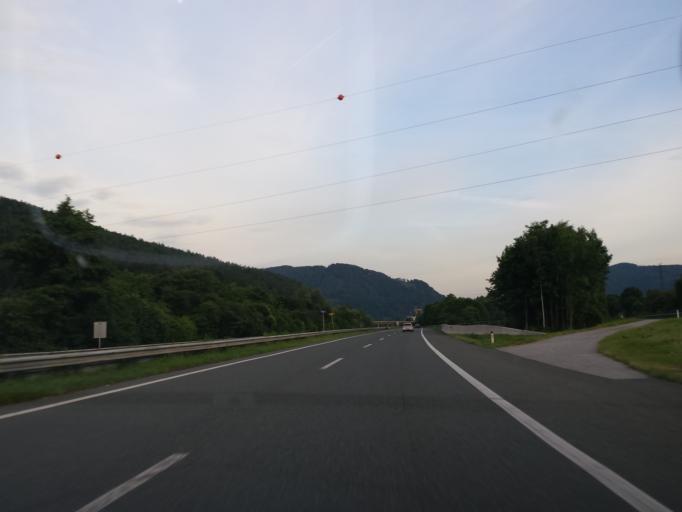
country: AT
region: Styria
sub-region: Politischer Bezirk Graz-Umgebung
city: Deutschfeistritz
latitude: 47.1859
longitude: 15.3314
